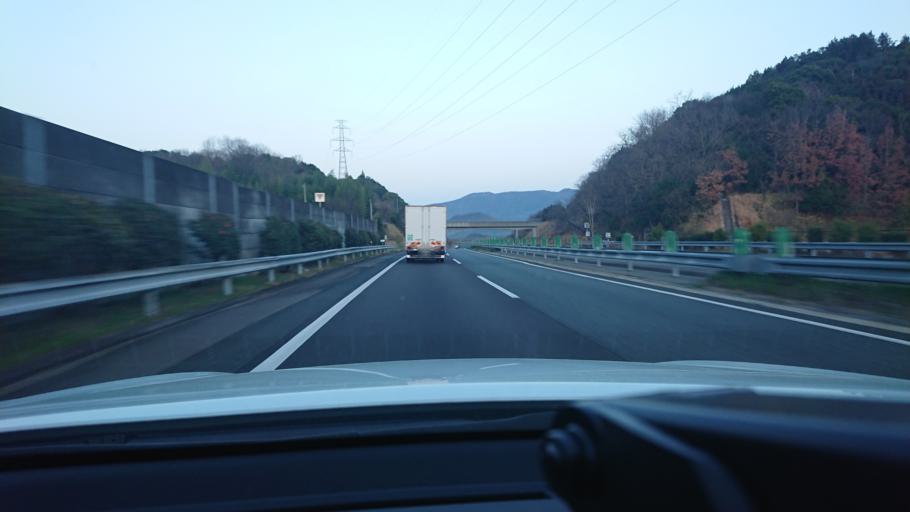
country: JP
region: Kagawa
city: Sakaidecho
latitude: 34.2707
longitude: 133.9422
